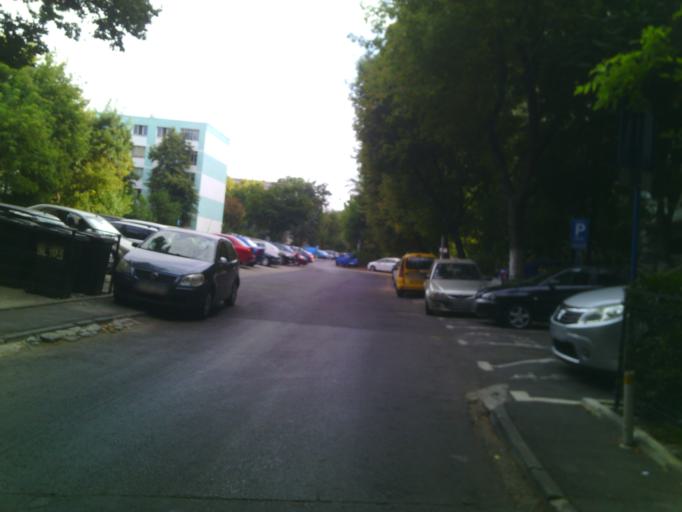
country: RO
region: Bucuresti
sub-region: Municipiul Bucuresti
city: Bucuresti
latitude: 44.3857
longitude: 26.0929
